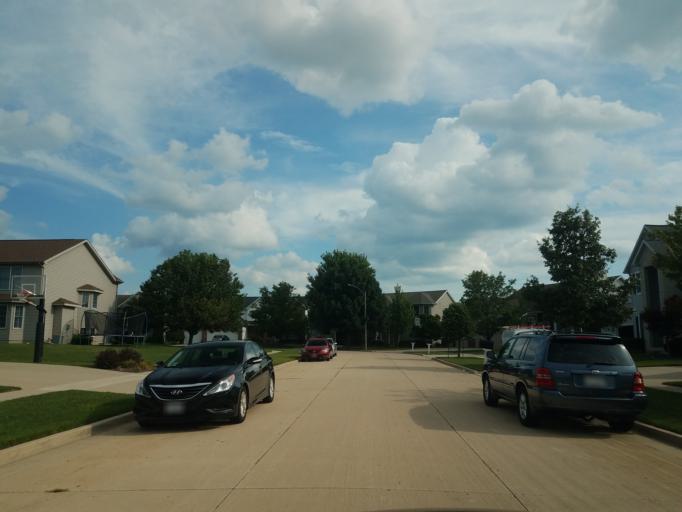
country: US
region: Illinois
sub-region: McLean County
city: Normal
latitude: 40.4990
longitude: -88.9182
